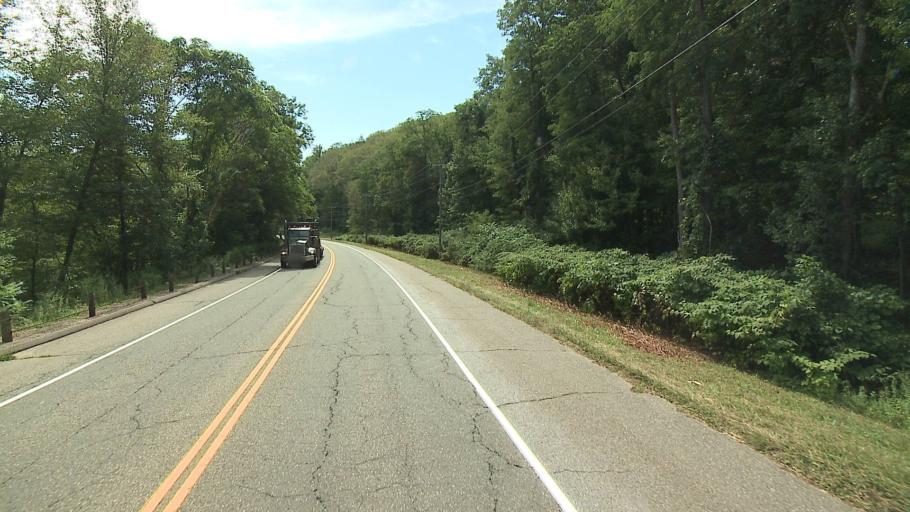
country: US
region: Connecticut
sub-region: Hartford County
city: Collinsville
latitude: 41.7888
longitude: -72.9254
